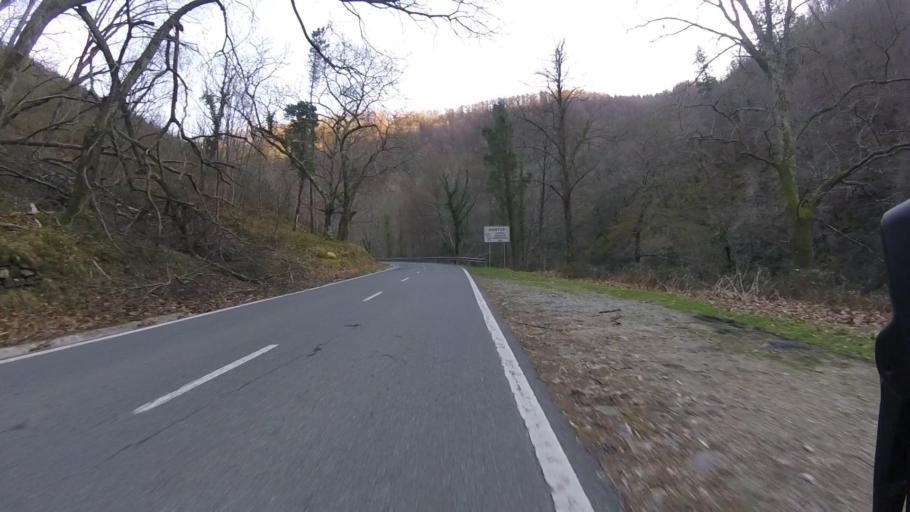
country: ES
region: Navarre
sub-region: Provincia de Navarra
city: Arano
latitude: 43.2085
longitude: -1.8683
